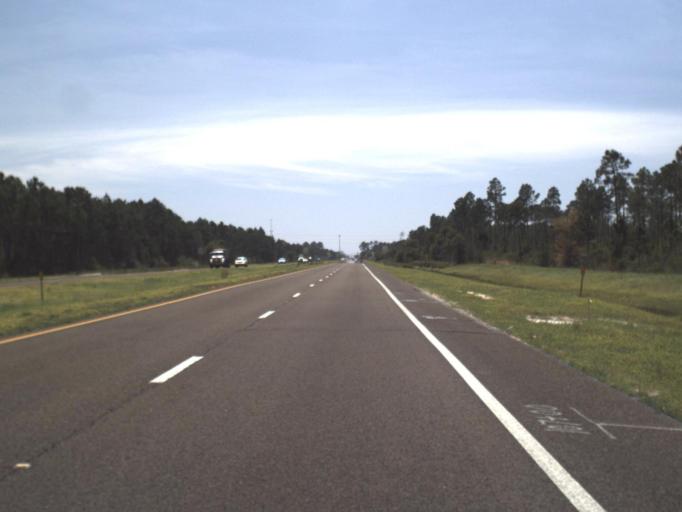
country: US
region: Florida
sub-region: Bay County
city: Laguna Beach
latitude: 30.2473
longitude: -85.8805
